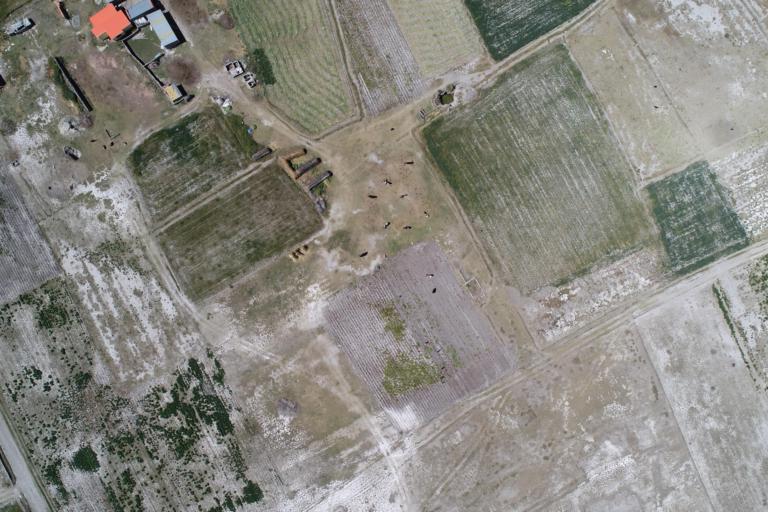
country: BO
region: La Paz
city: Achacachi
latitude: -16.0116
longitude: -68.7270
